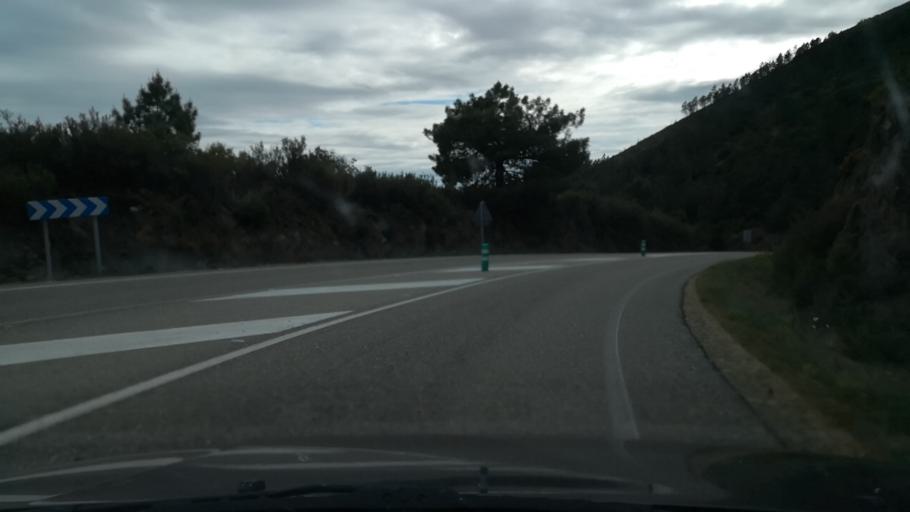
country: ES
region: Extremadura
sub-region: Provincia de Caceres
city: Acebo
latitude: 40.2220
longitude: -6.6730
